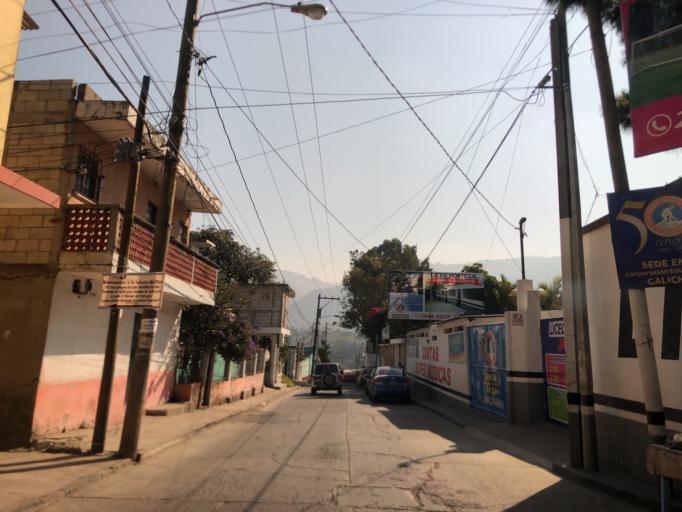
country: GT
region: Guatemala
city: Santa Catarina Pinula
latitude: 14.5407
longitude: -90.5245
